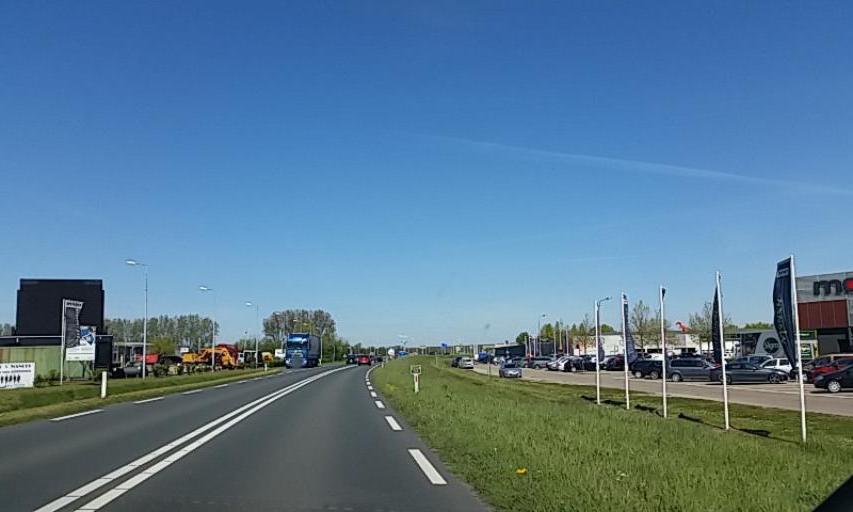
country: NL
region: Zeeland
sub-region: Gemeente Hulst
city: Hulst
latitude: 51.2714
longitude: 4.0440
